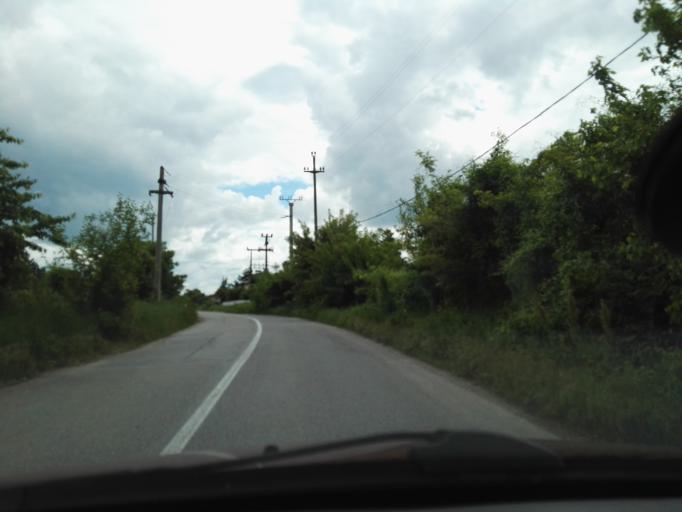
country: RO
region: Ilfov
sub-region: Comuna Copaceni
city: Copaceni
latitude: 44.2367
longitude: 26.1144
